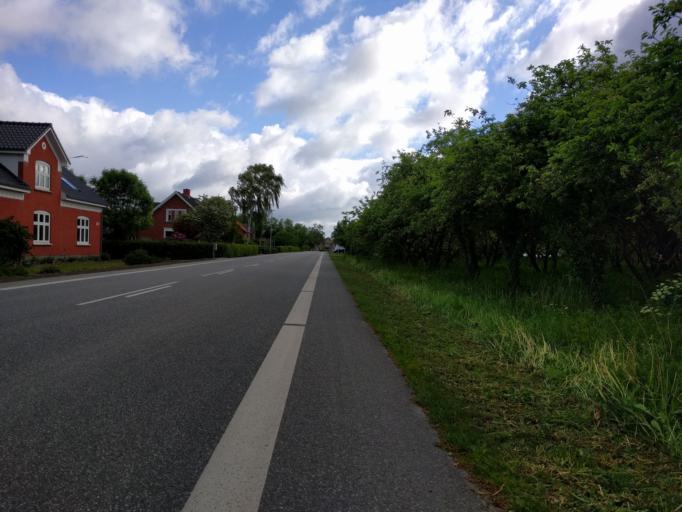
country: DK
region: South Denmark
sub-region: Nyborg Kommune
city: Ullerslev
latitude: 55.4067
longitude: 10.6211
